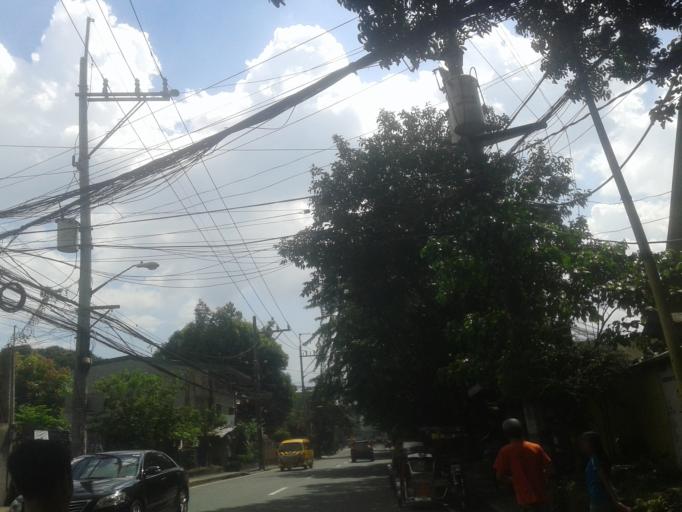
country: PH
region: Metro Manila
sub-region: Mandaluyong
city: Mandaluyong City
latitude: 14.5847
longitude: 121.0449
